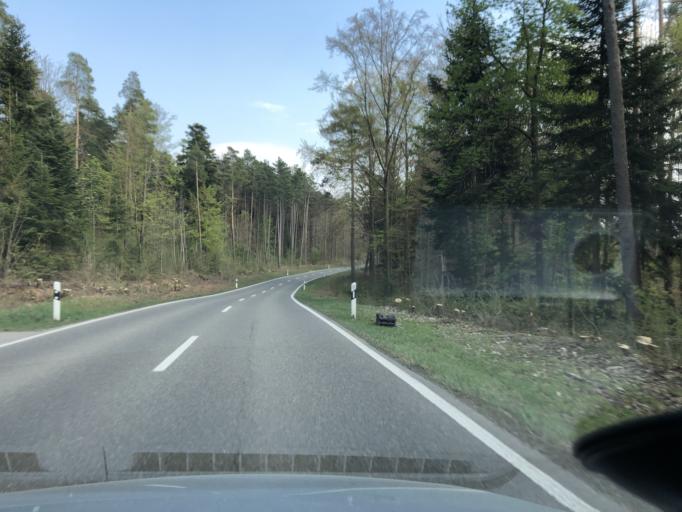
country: DE
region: Baden-Wuerttemberg
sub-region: Karlsruhe Region
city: Simmozheim
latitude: 48.7610
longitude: 8.8324
